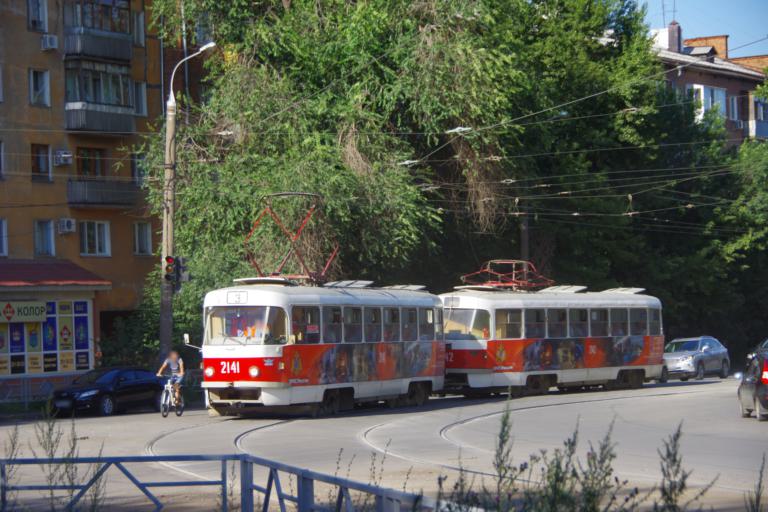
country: RU
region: Samara
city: Samara
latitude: 53.2015
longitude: 50.2274
